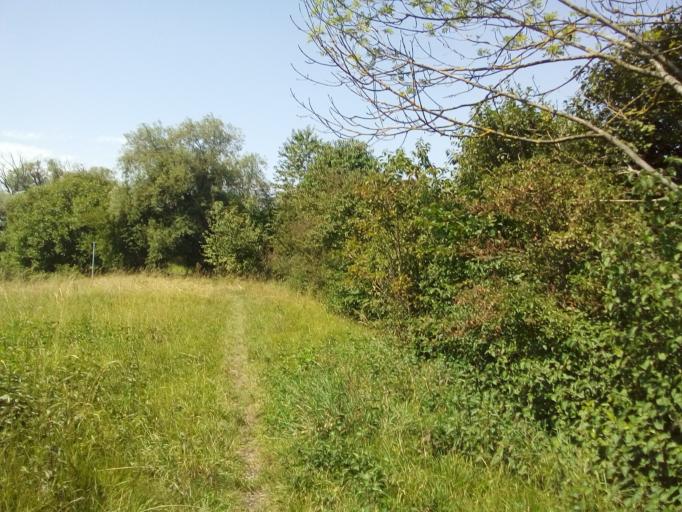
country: DE
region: Bavaria
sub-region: Upper Bavaria
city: Unterfoehring
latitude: 48.1749
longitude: 11.6555
